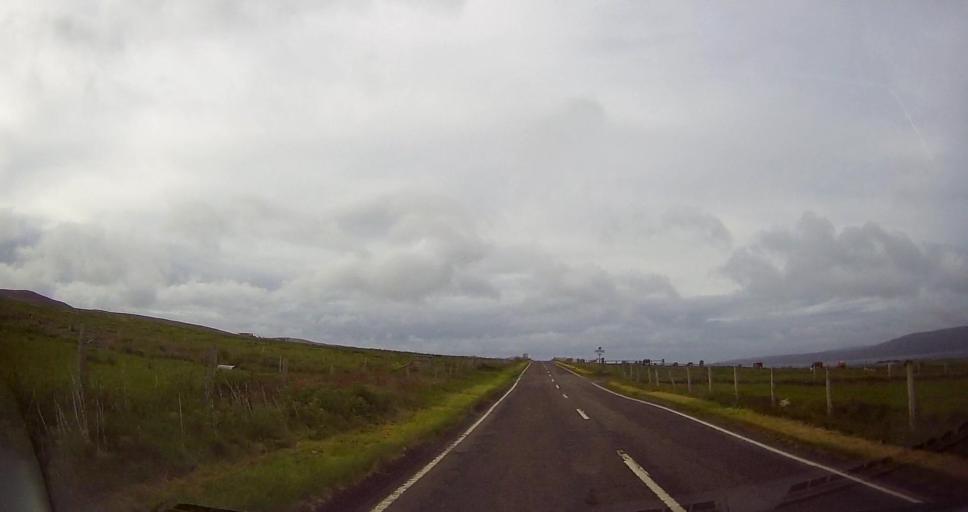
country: GB
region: Scotland
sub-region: Orkney Islands
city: Stromness
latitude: 58.9489
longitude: -3.2160
